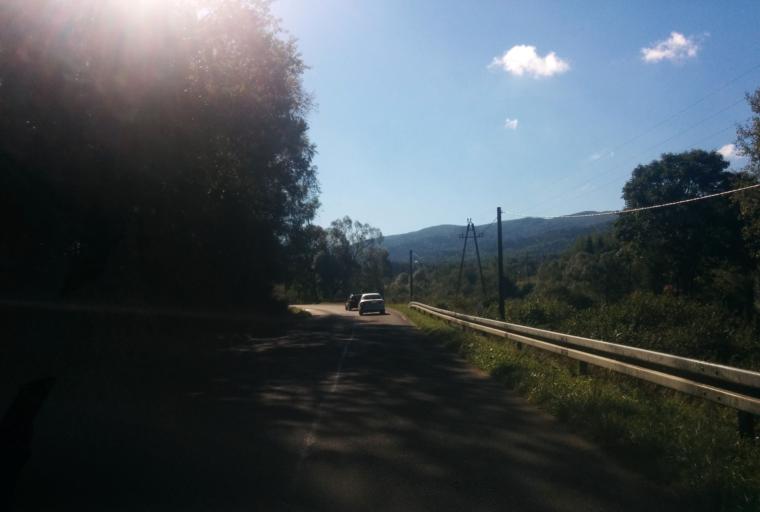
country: PL
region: Subcarpathian Voivodeship
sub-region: Powiat leski
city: Cisna
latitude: 49.2013
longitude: 22.3654
